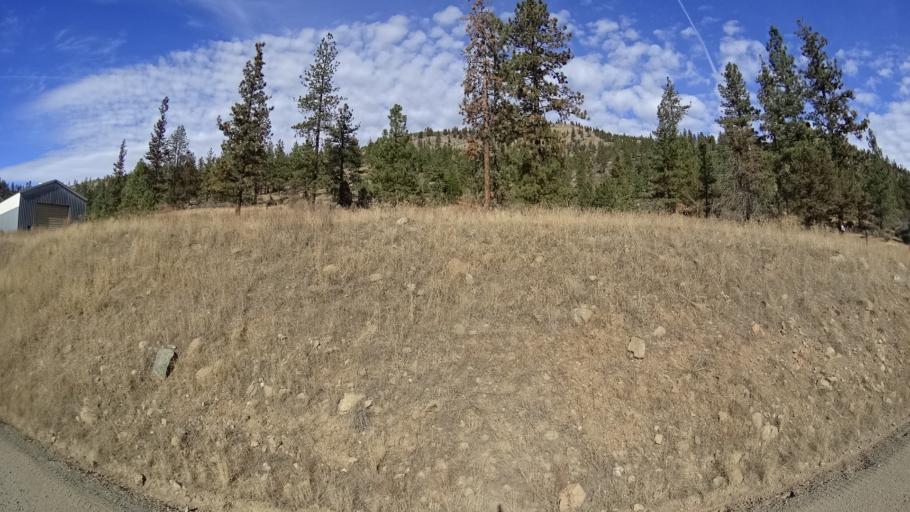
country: US
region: California
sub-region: Siskiyou County
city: Yreka
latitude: 41.6102
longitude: -122.7319
